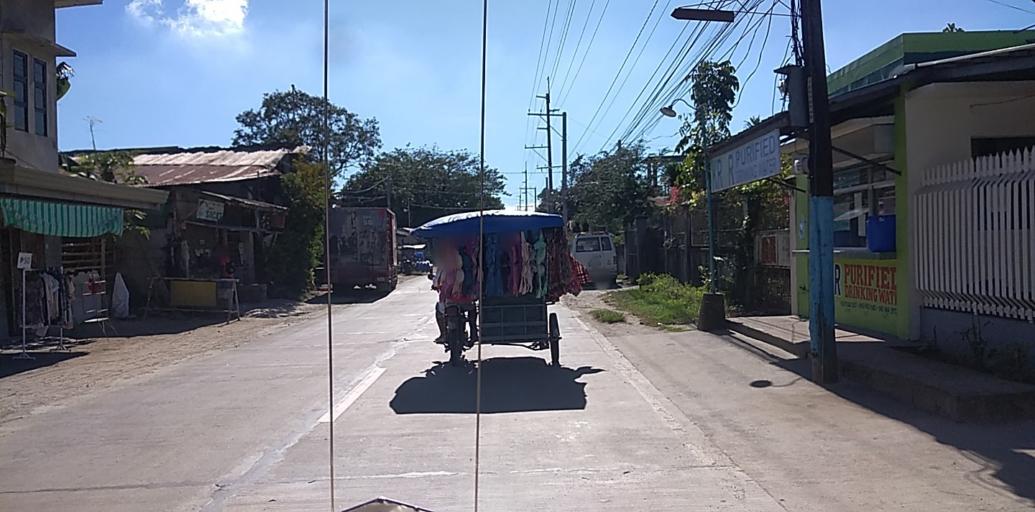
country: PH
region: Central Luzon
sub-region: Province of Pampanga
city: San Luis
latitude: 15.0562
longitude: 120.7770
